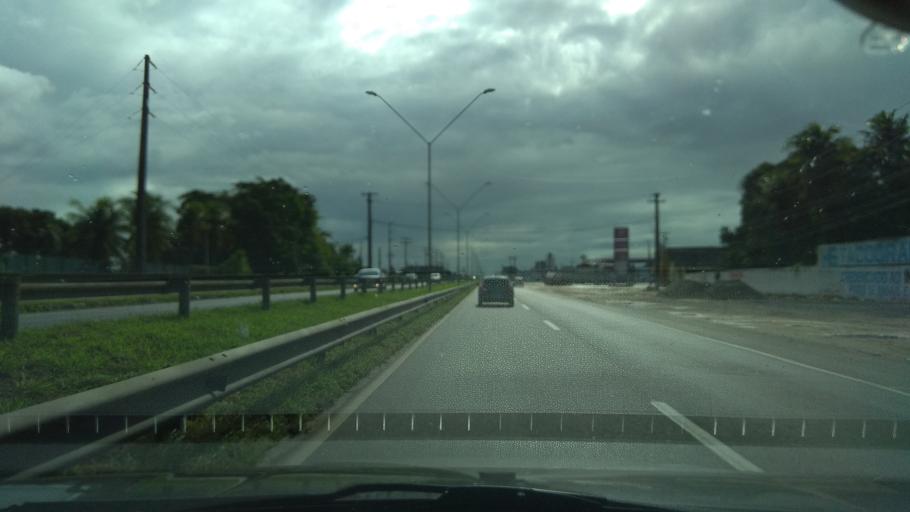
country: BR
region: Bahia
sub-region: Feira De Santana
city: Feira de Santana
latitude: -12.3124
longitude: -38.8830
